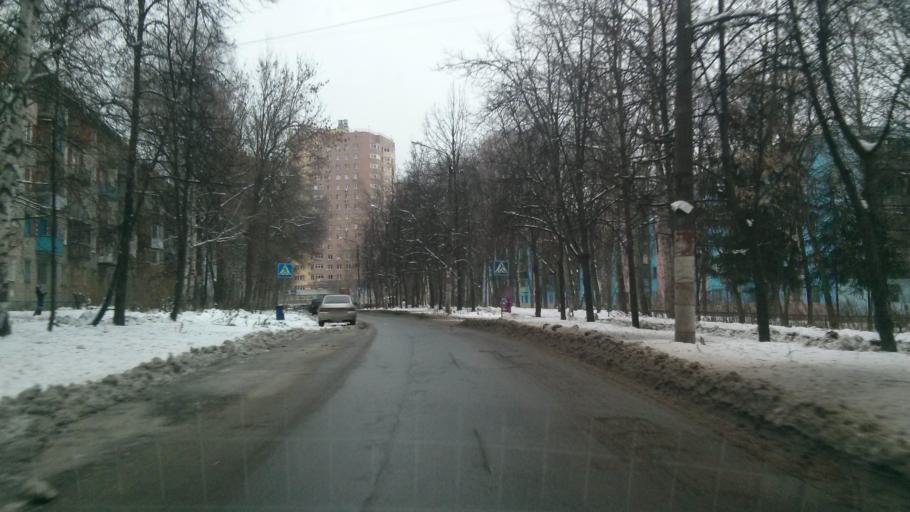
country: RU
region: Nizjnij Novgorod
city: Nizhniy Novgorod
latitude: 56.2918
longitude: 44.0435
